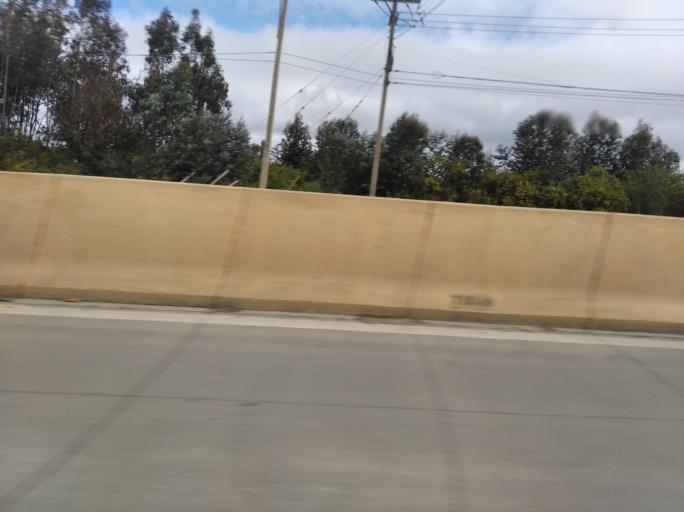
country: CL
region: Valparaiso
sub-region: Provincia de Valparaiso
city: Valparaiso
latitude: -33.0958
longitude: -71.5872
